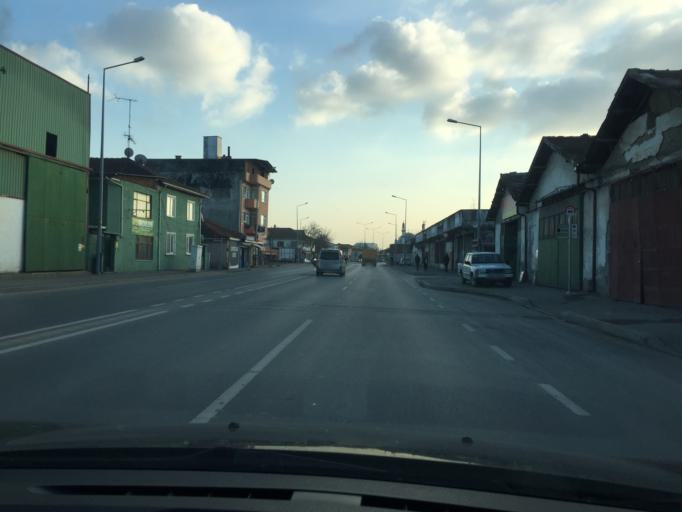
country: TR
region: Sakarya
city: Adapazari
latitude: 40.7929
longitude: 30.4072
